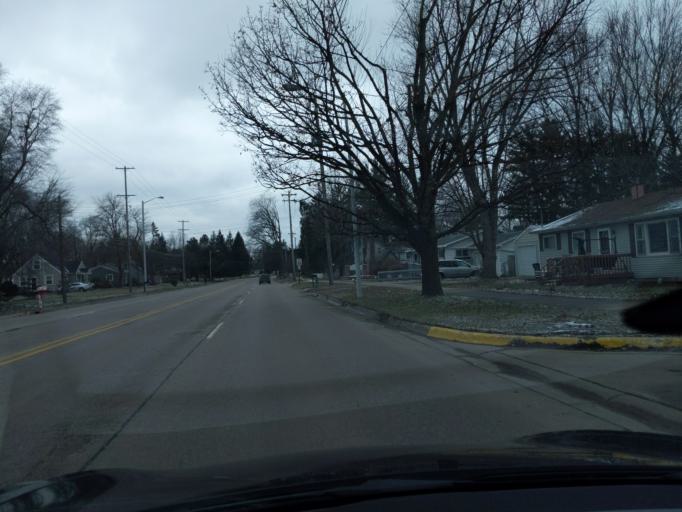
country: US
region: Michigan
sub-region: Ingham County
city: East Lansing
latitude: 42.7594
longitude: -84.4892
